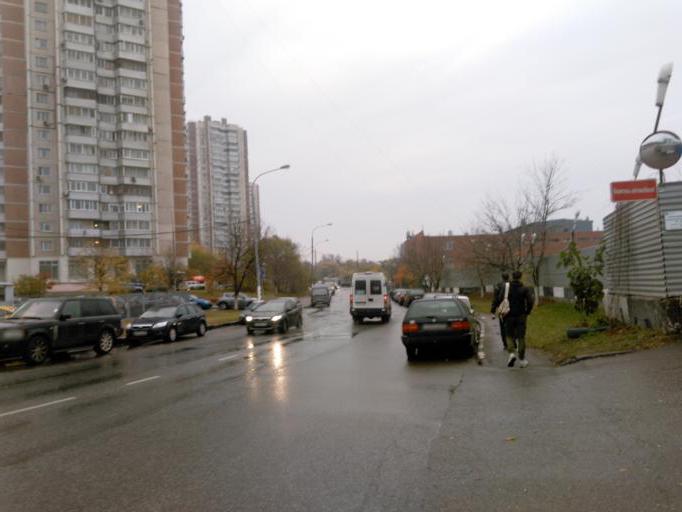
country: RU
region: Moscow
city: Yasenevo
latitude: 55.6007
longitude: 37.5074
